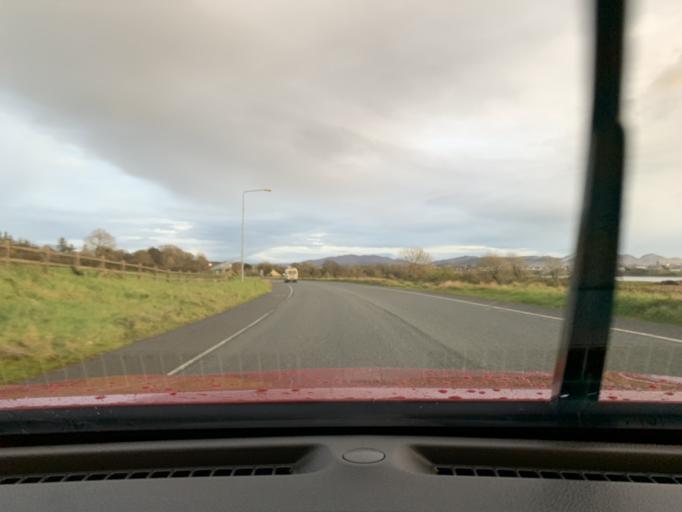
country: IE
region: Connaught
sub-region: Sligo
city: Sligo
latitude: 54.2940
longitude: -8.4912
